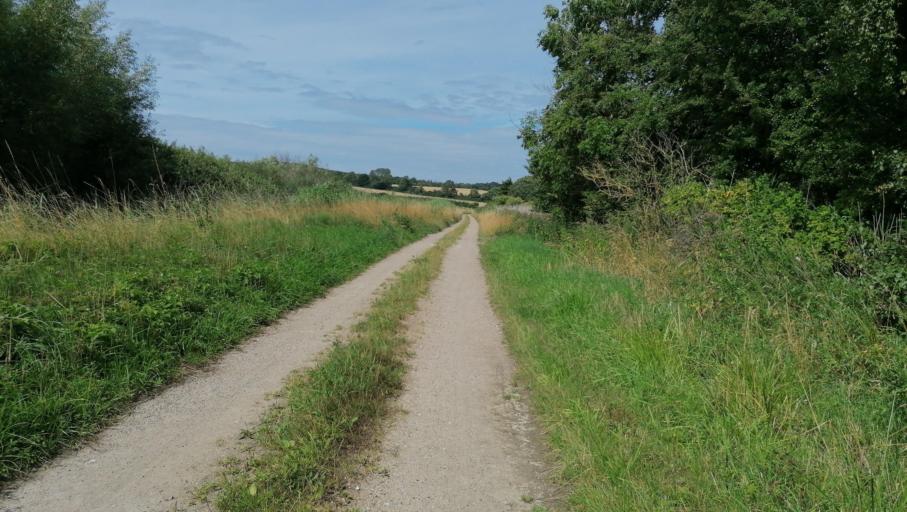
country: DK
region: Zealand
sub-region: Odsherred Kommune
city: Horve
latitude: 55.7794
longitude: 11.4200
